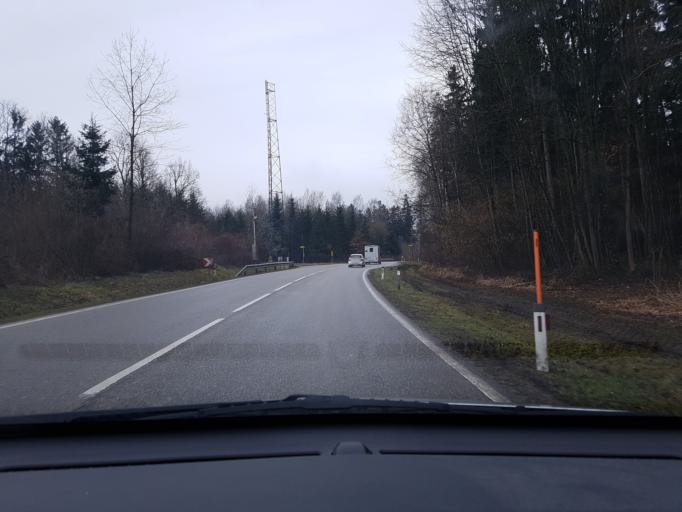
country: AT
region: Upper Austria
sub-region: Steyr Stadt
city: Steyr
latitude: 48.0635
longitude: 14.3886
